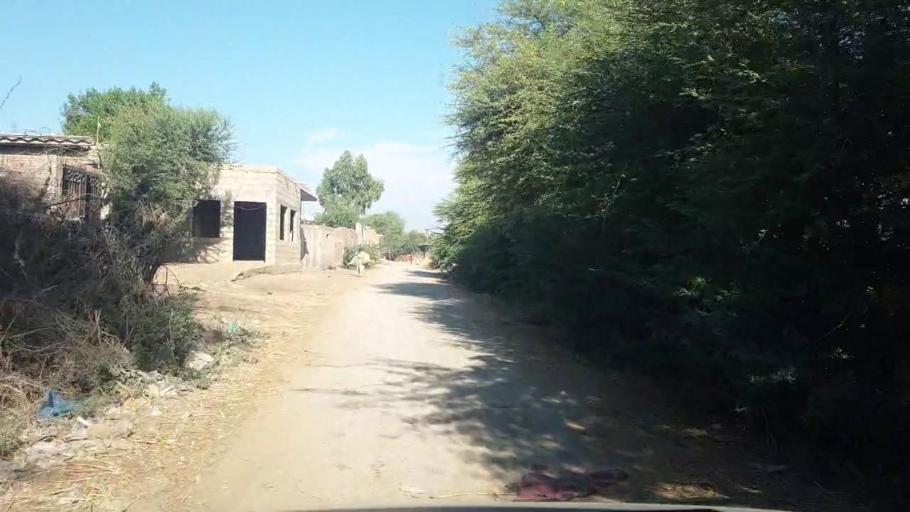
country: PK
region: Sindh
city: Talhar
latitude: 24.8905
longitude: 68.8143
